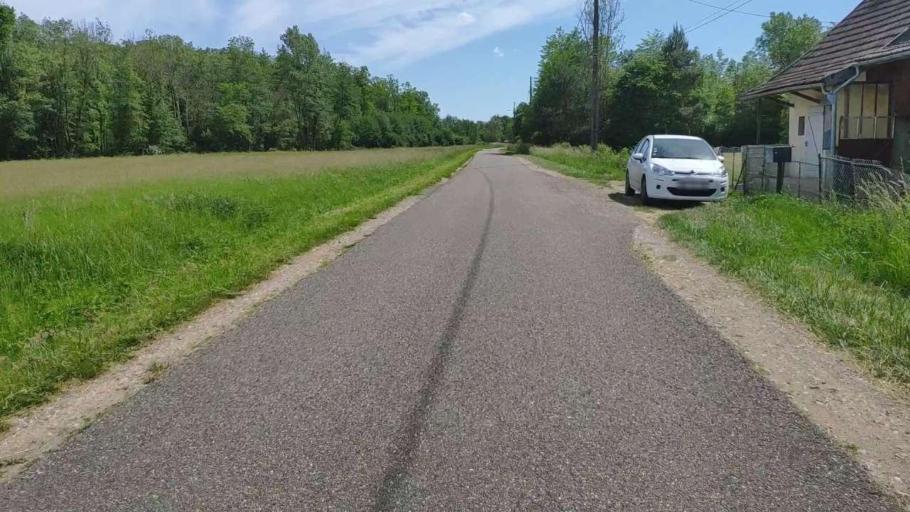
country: FR
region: Franche-Comte
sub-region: Departement du Jura
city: Bletterans
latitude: 46.7204
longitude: 5.4765
